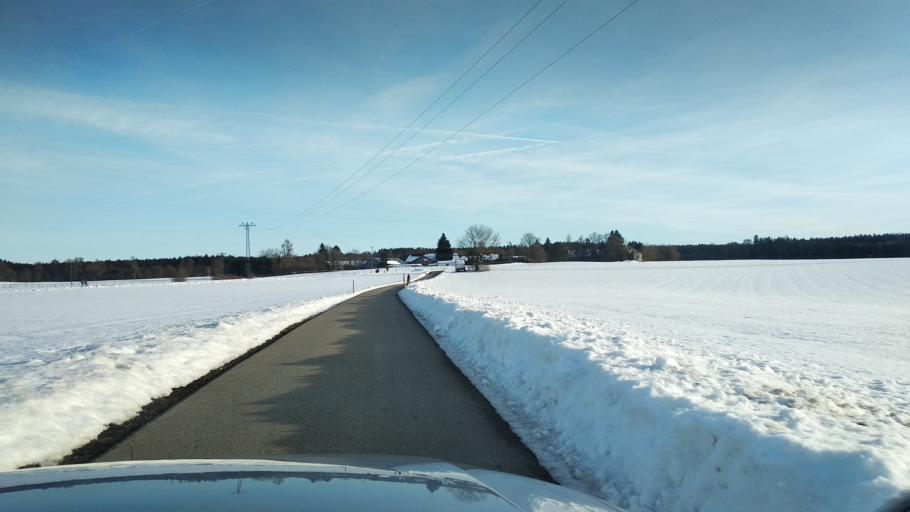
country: DE
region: Bavaria
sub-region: Upper Bavaria
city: Kirchseeon
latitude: 48.0739
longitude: 11.8655
